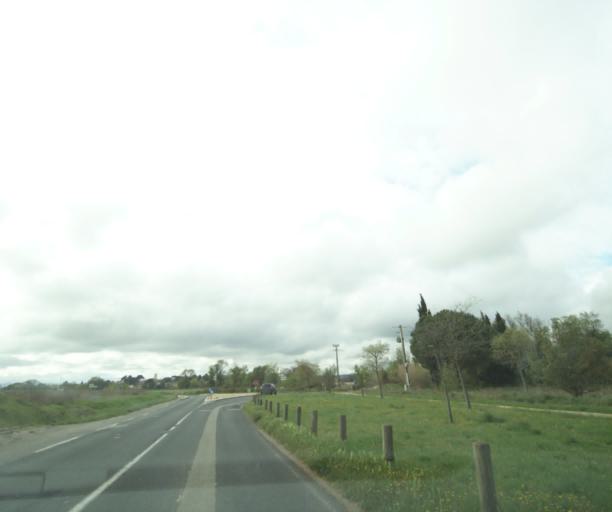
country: FR
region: Languedoc-Roussillon
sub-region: Departement de l'Herault
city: Saussan
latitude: 43.5683
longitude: 3.7849
